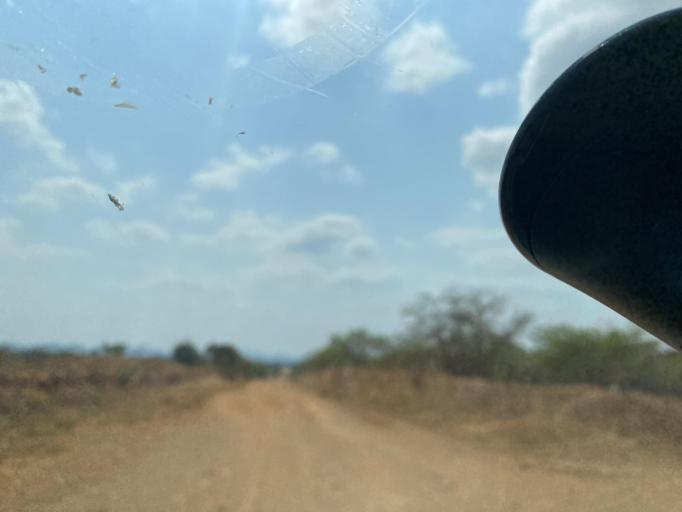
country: ZM
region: Lusaka
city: Chongwe
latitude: -15.5912
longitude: 28.7836
